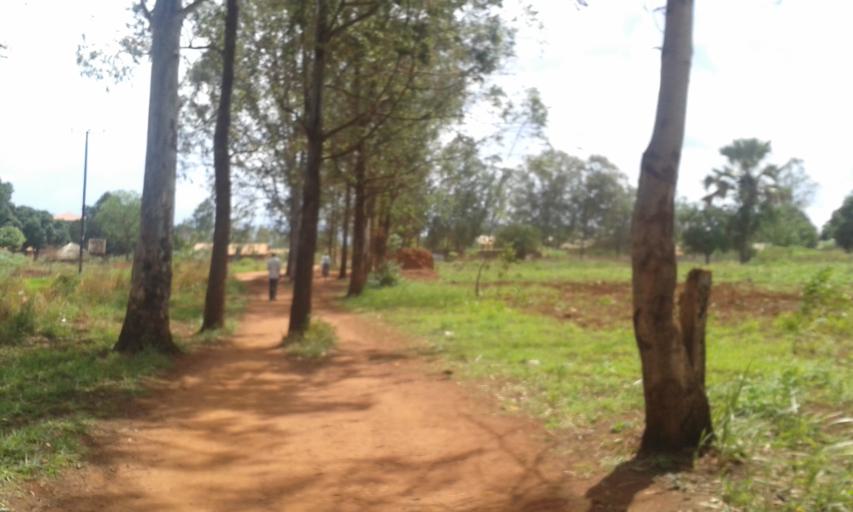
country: UG
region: Northern Region
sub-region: Gulu District
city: Gulu
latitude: 2.7881
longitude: 32.3196
